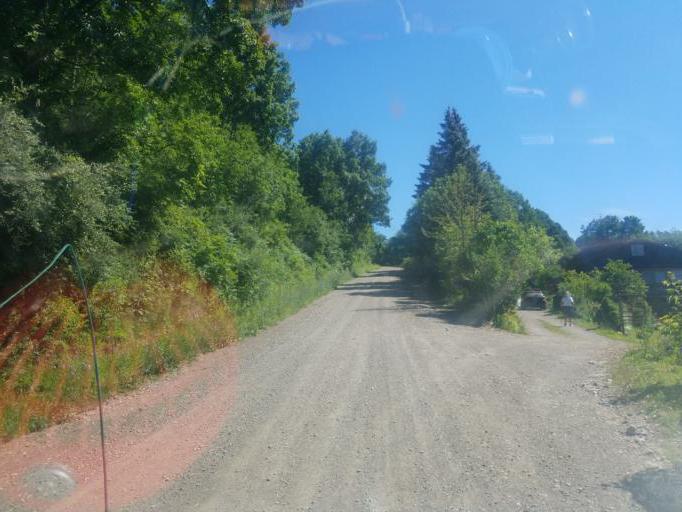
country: US
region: New York
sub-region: Ontario County
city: Naples
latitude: 42.6621
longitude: -77.3442
